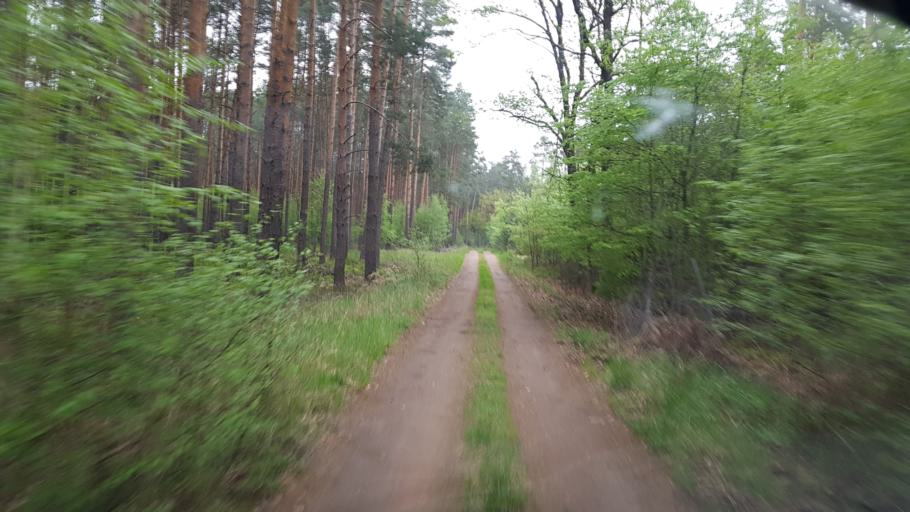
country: DE
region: Brandenburg
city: Hohenbucko
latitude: 51.7128
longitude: 13.5249
